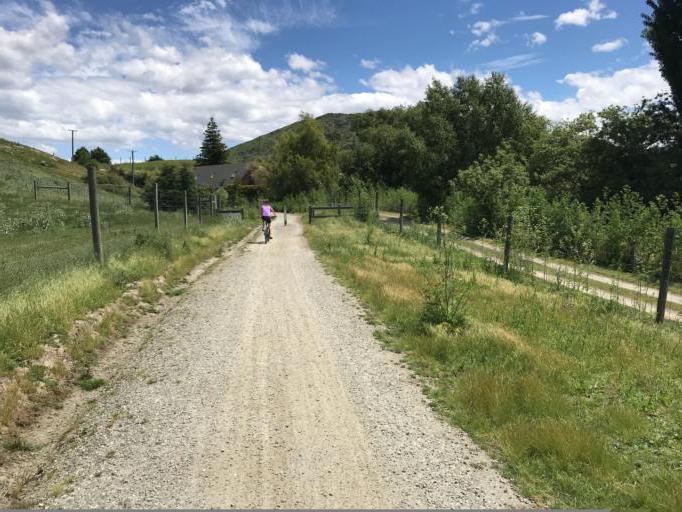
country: NZ
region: Otago
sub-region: Queenstown-Lakes District
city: Arrowtown
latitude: -44.9930
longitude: 168.8576
